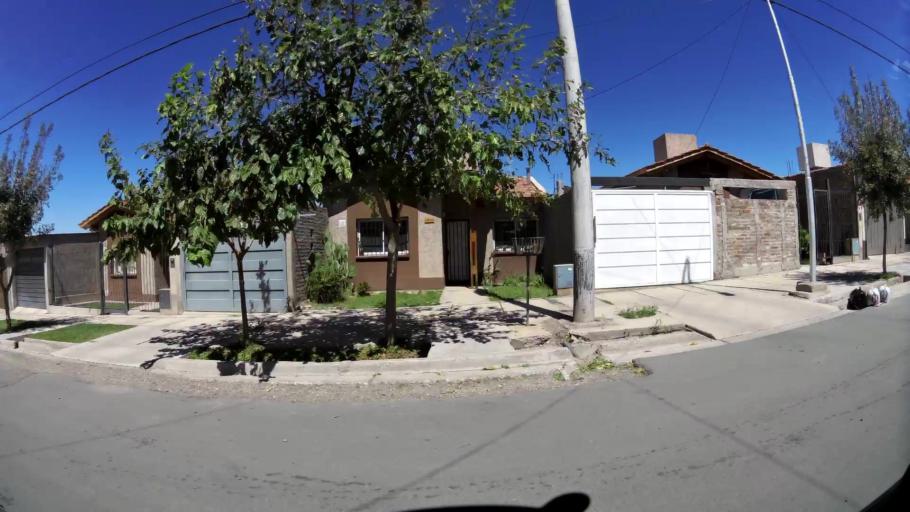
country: AR
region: Mendoza
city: Las Heras
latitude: -32.8506
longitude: -68.8556
